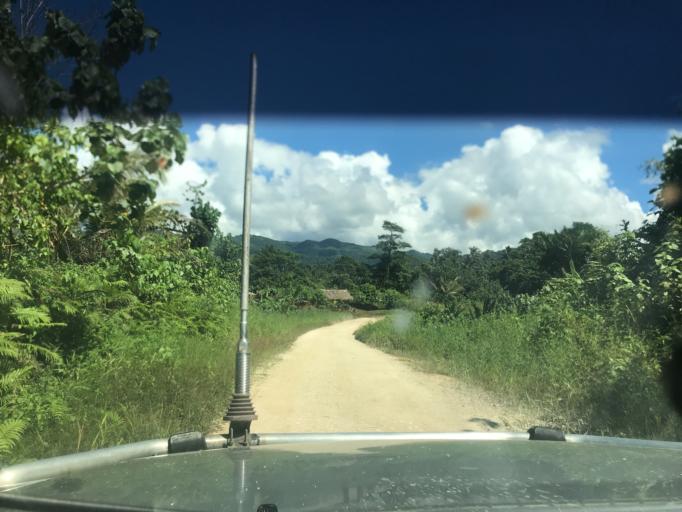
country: SB
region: Malaita
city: Auki
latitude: -8.7275
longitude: 160.9034
